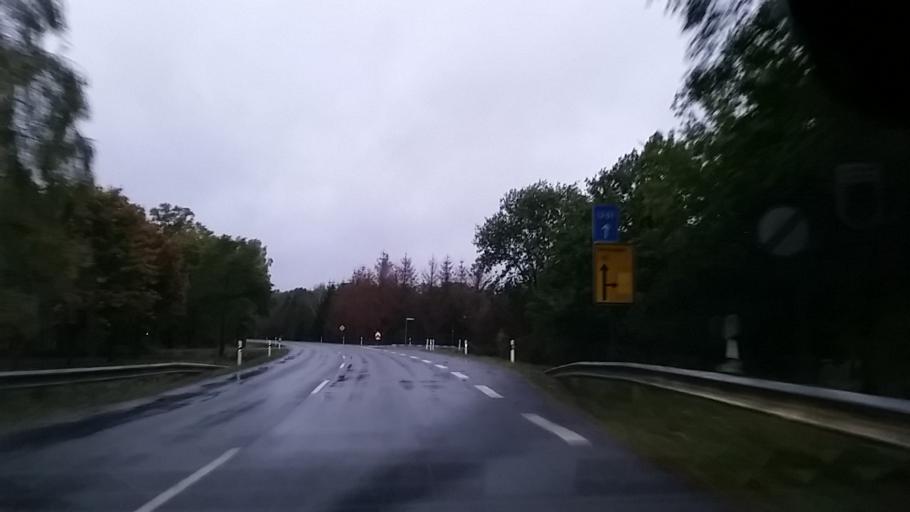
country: DE
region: Lower Saxony
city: Weyhausen
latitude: 52.4529
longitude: 10.7119
